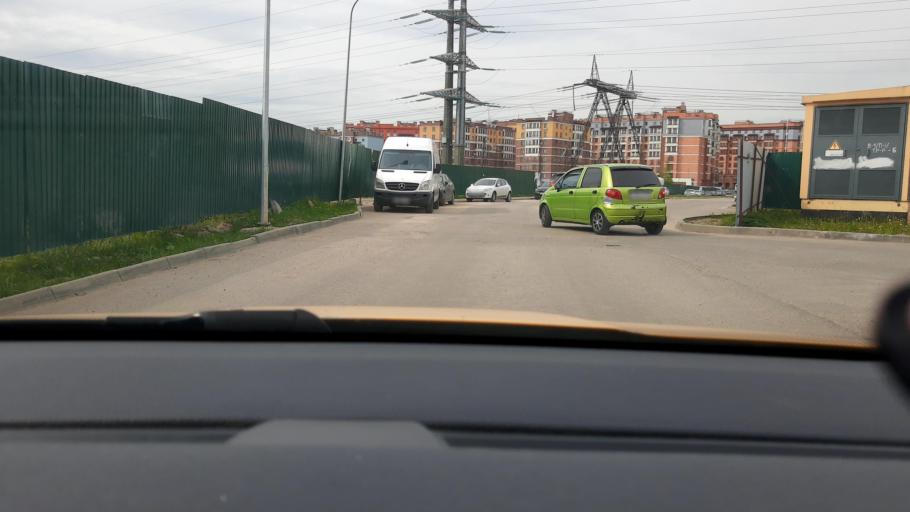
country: RU
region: Moskovskaya
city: Opalikha
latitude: 55.8815
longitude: 37.2686
